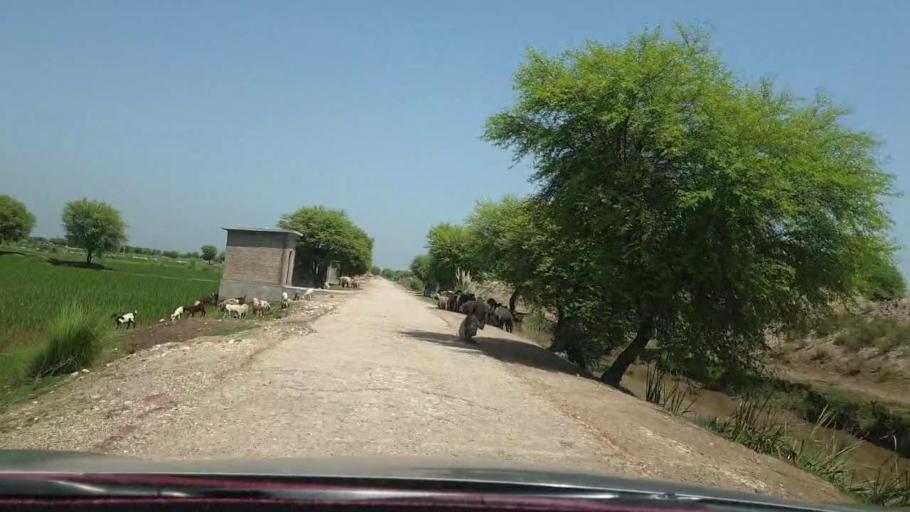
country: PK
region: Sindh
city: Warah
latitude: 27.5108
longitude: 67.7985
